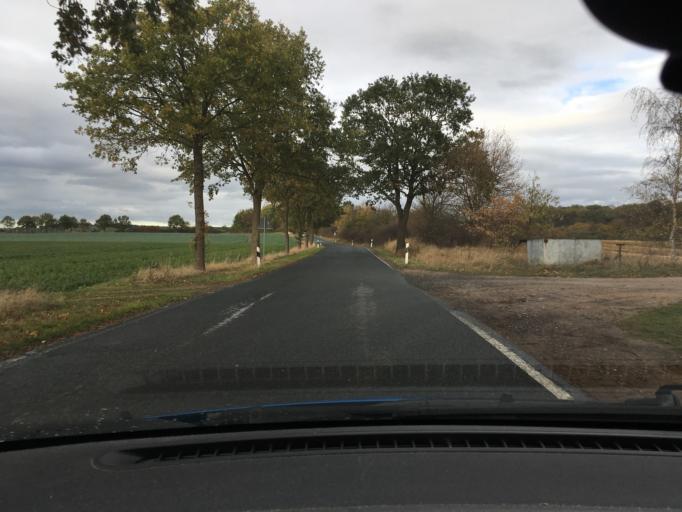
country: DE
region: Schleswig-Holstein
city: Fredeburg
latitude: 53.6504
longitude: 10.6943
